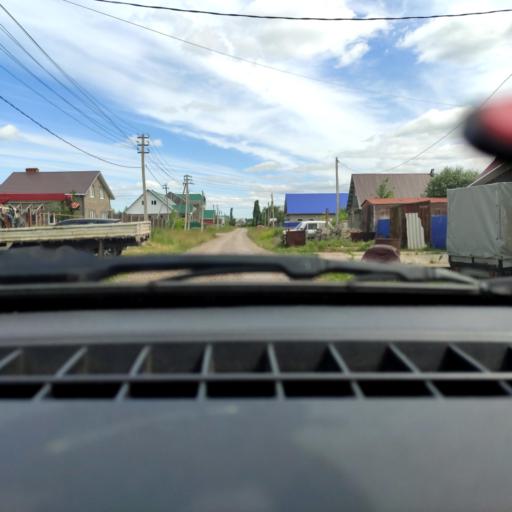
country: RU
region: Bashkortostan
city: Iglino
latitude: 54.7864
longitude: 56.2428
